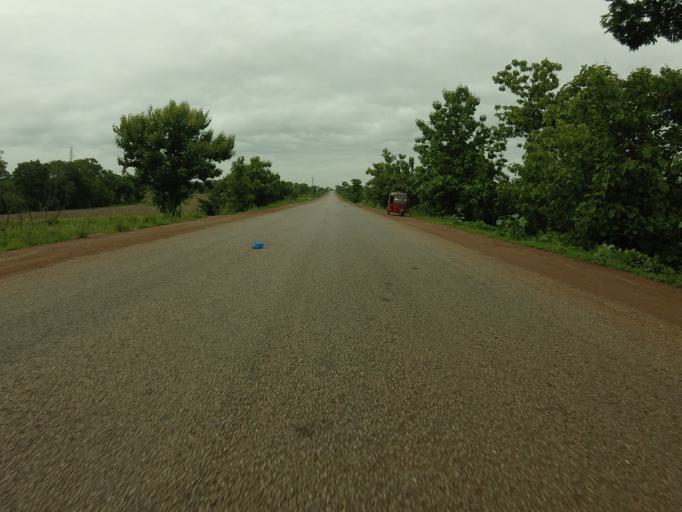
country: GH
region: Northern
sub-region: Yendi
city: Yendi
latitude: 9.4935
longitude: -0.0215
